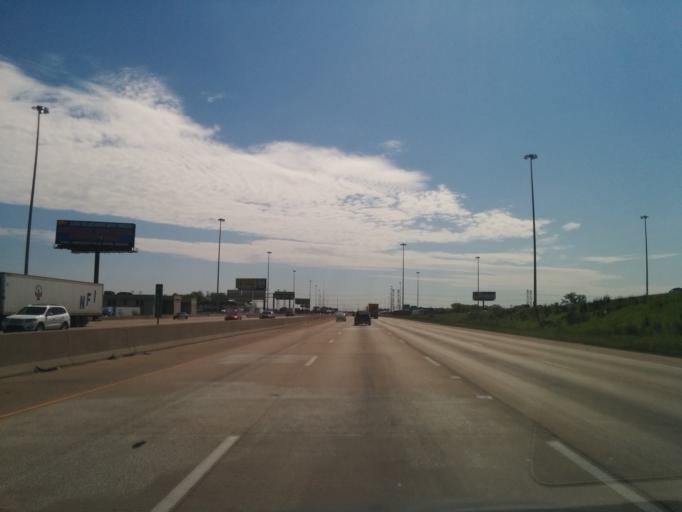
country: US
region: Illinois
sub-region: Cook County
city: Thornton
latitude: 41.5777
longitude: -87.5741
